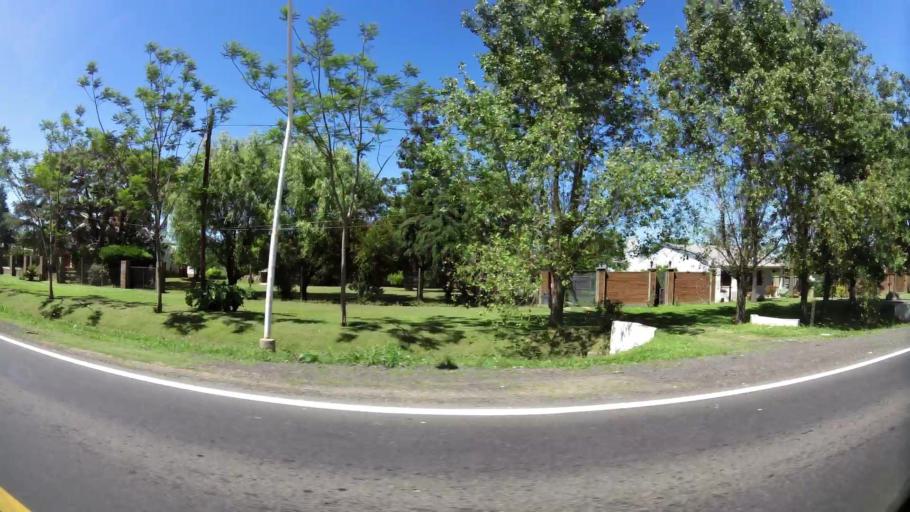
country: AR
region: Santa Fe
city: Esperanza
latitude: -31.4368
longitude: -60.9541
